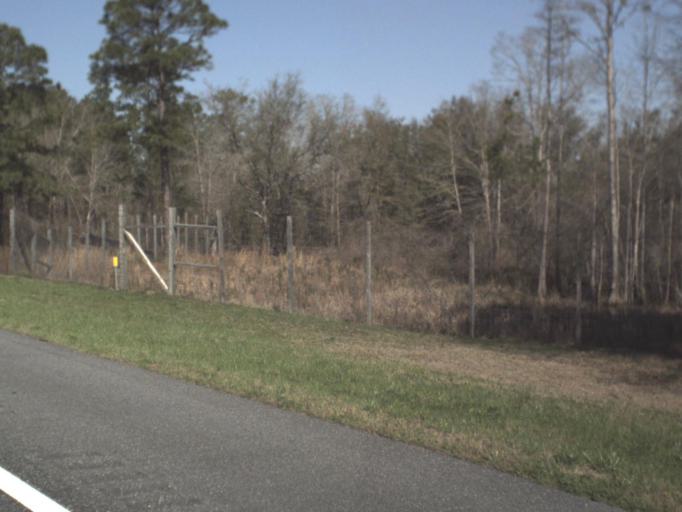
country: US
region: Florida
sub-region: Jackson County
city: Marianna
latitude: 30.6990
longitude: -85.1325
